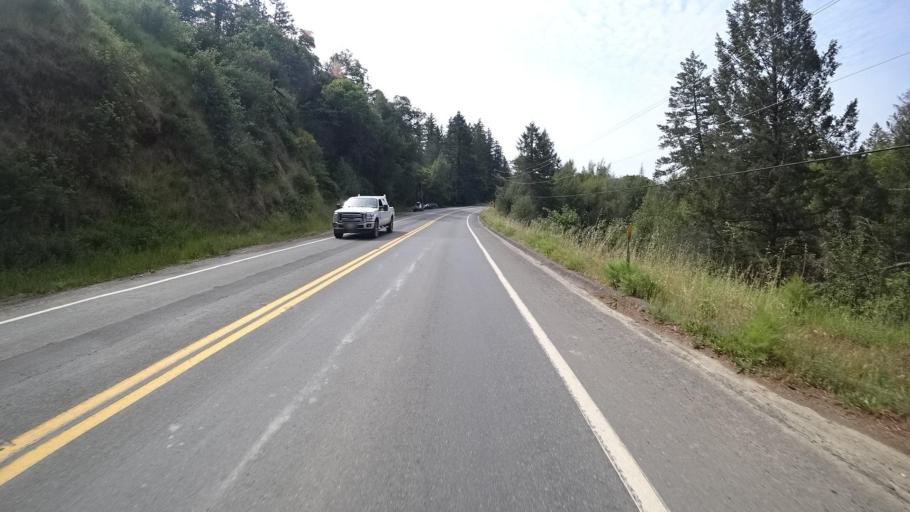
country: US
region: California
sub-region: Humboldt County
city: Redway
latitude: 40.1135
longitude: -123.7946
